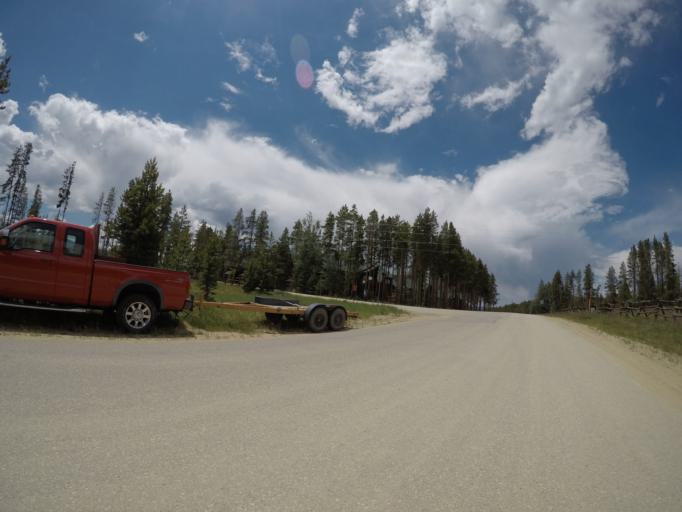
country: US
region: Colorado
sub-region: Grand County
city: Fraser
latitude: 39.9514
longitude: -105.7888
